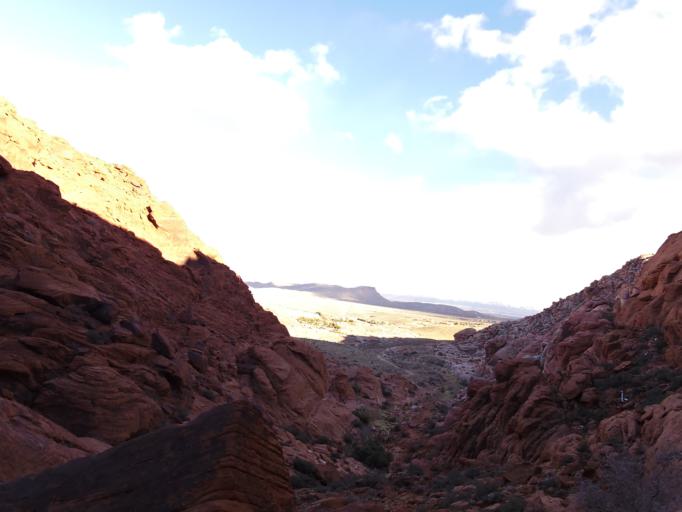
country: US
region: Nevada
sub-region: Clark County
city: Summerlin South
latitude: 36.1525
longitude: -115.4298
